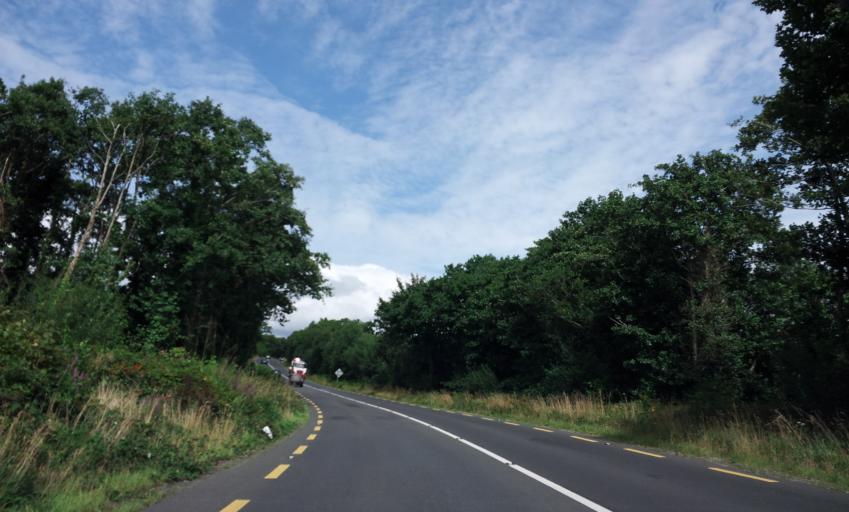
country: IE
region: Munster
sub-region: Ciarrai
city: Killorglin
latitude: 52.0994
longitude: -9.8252
